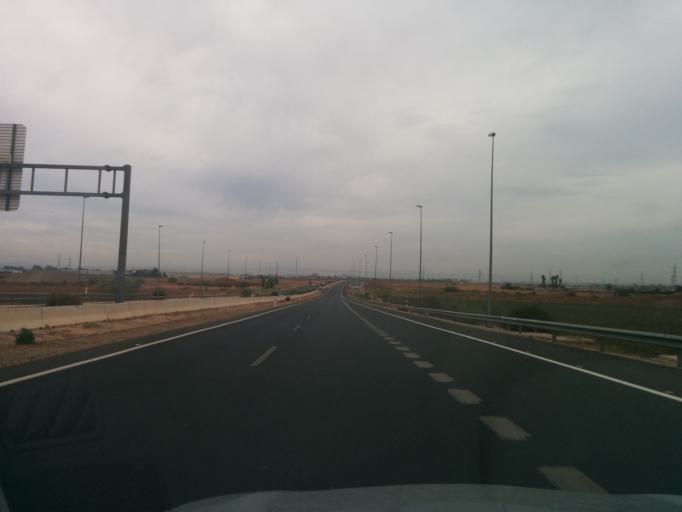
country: ES
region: Andalusia
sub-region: Provincia de Sevilla
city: La Algaba
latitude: 37.4401
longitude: -5.9716
